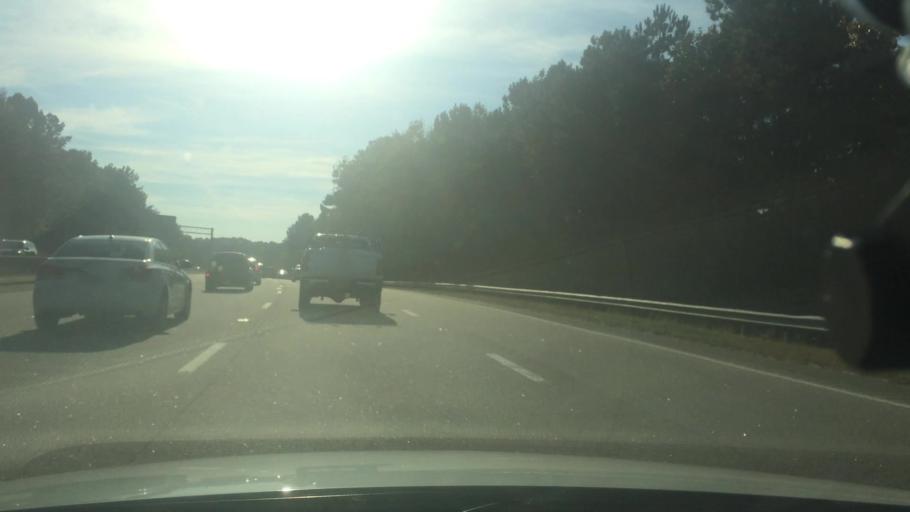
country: US
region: North Carolina
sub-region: Wake County
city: West Raleigh
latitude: 35.8332
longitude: -78.6756
